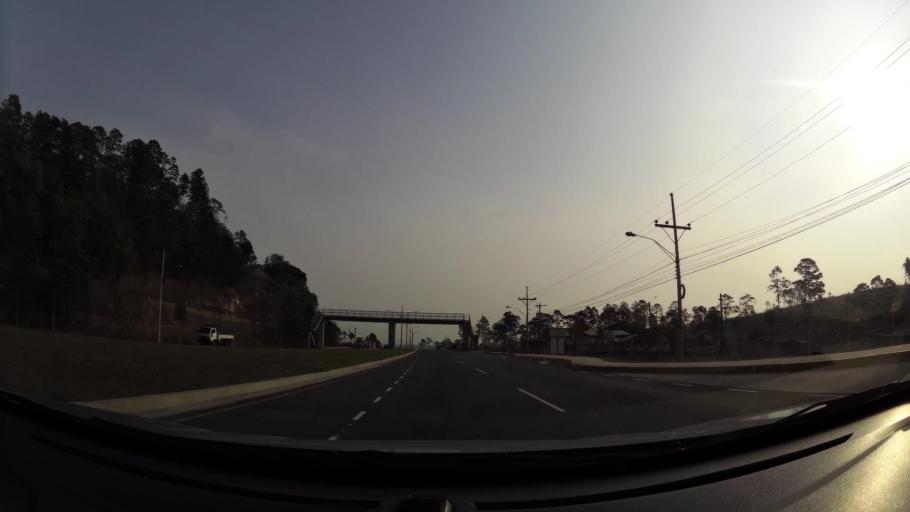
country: HN
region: Francisco Morazan
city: Tamara
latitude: 14.1743
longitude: -87.3124
